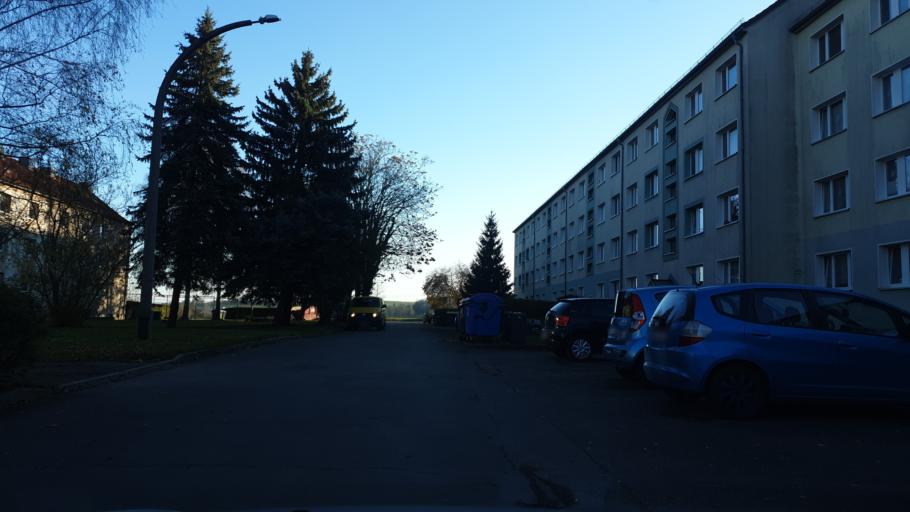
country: DE
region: Thuringia
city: Hartmannsdorf
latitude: 50.9732
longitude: 11.9702
